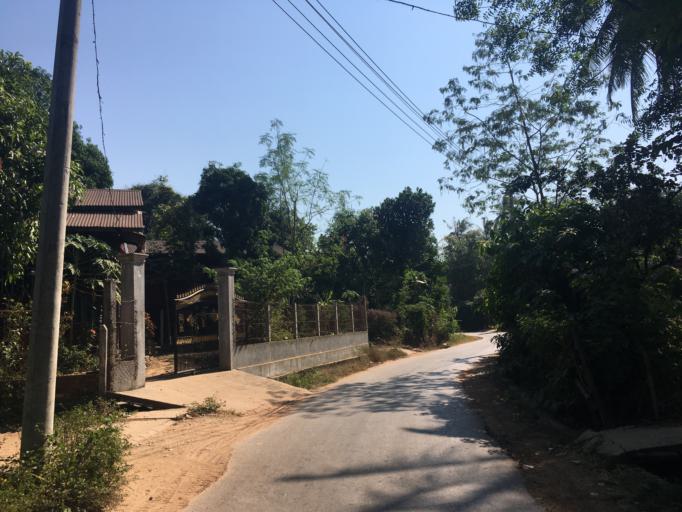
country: MM
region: Mon
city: Mawlamyine
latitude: 16.4320
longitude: 97.7033
